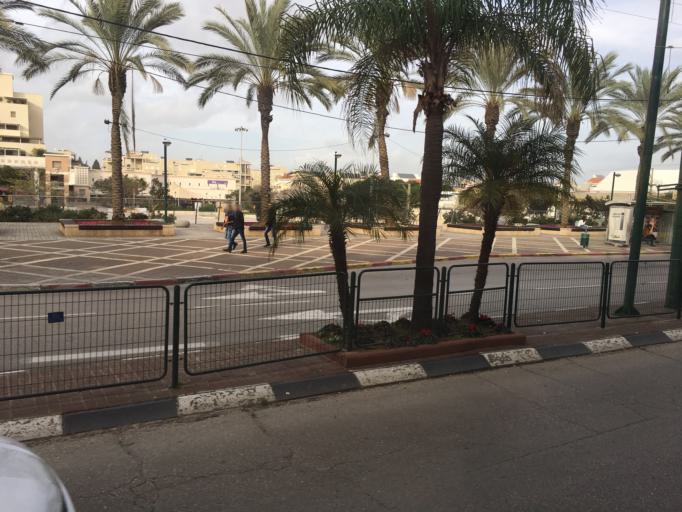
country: IL
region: Central District
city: Kfar Saba
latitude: 32.1765
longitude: 34.9034
